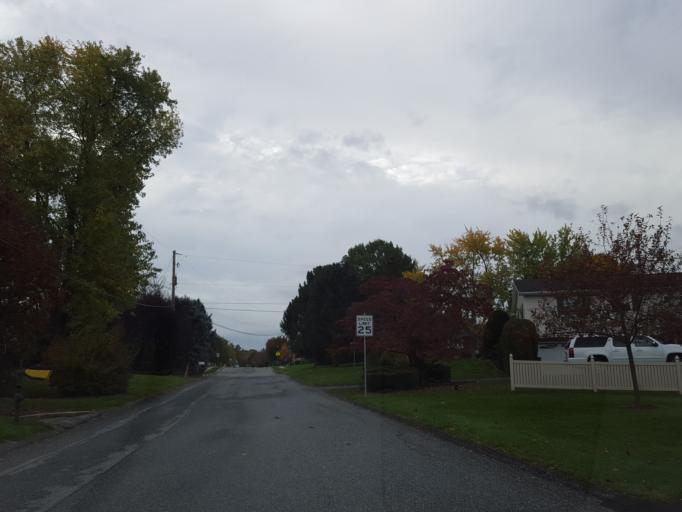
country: US
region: Pennsylvania
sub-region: York County
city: Spry
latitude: 39.9305
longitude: -76.6647
